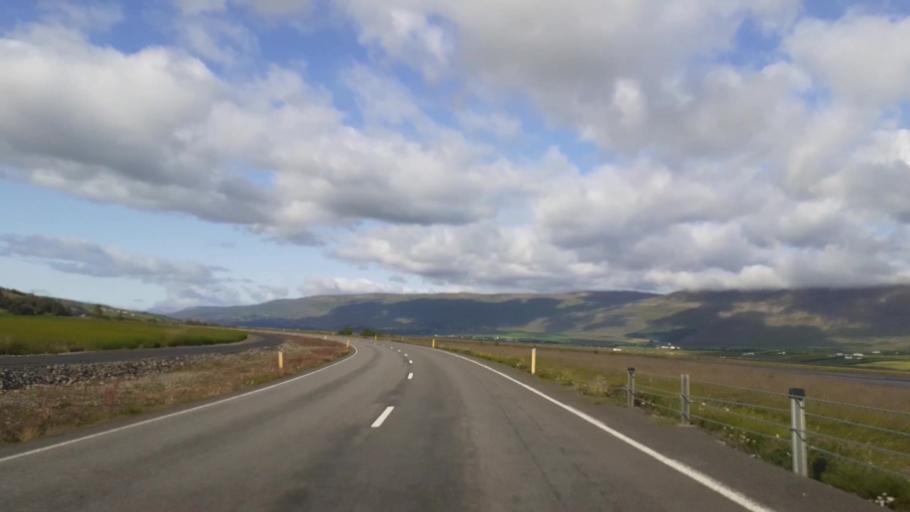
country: IS
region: Northeast
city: Akureyri
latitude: 65.5925
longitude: -18.0789
